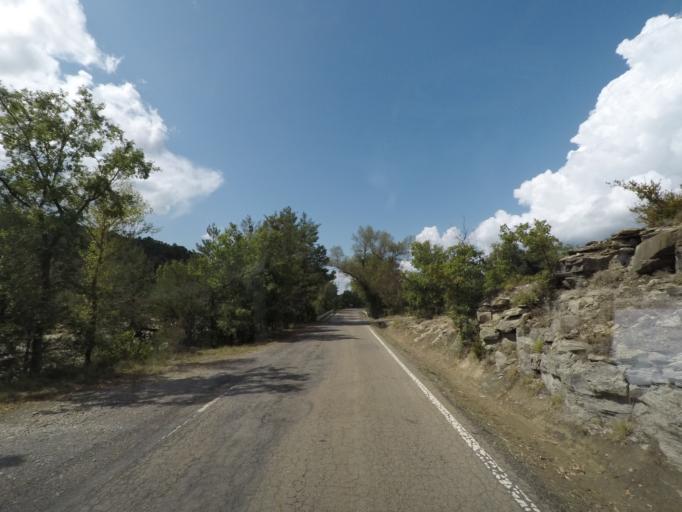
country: ES
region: Aragon
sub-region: Provincia de Huesca
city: Yebra de Basa
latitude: 42.3940
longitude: -0.3233
